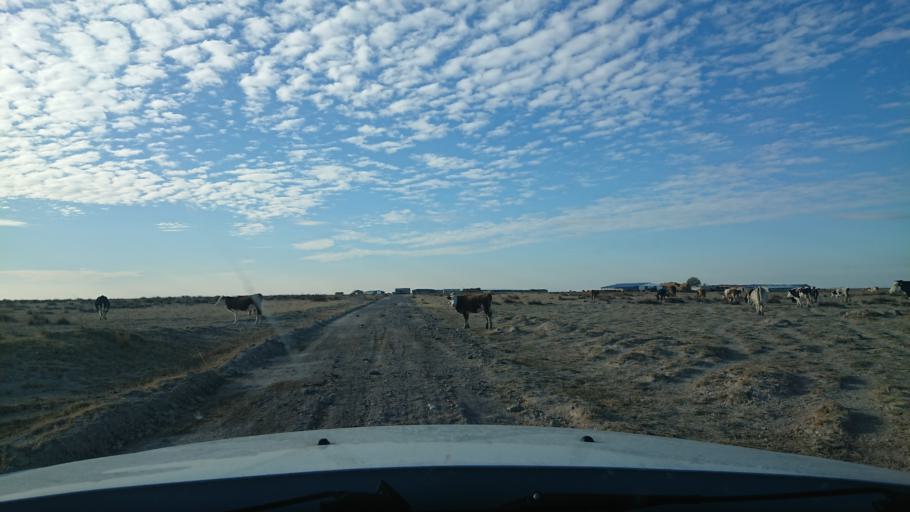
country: TR
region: Aksaray
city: Eskil
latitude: 38.5662
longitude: 33.2987
